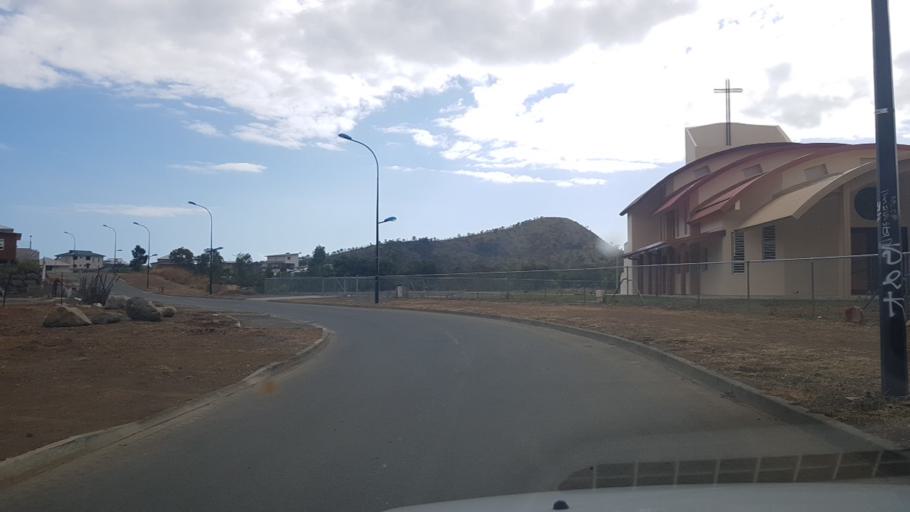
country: NC
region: South Province
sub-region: Dumbea
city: Dumbea
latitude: -22.1978
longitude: 166.4426
